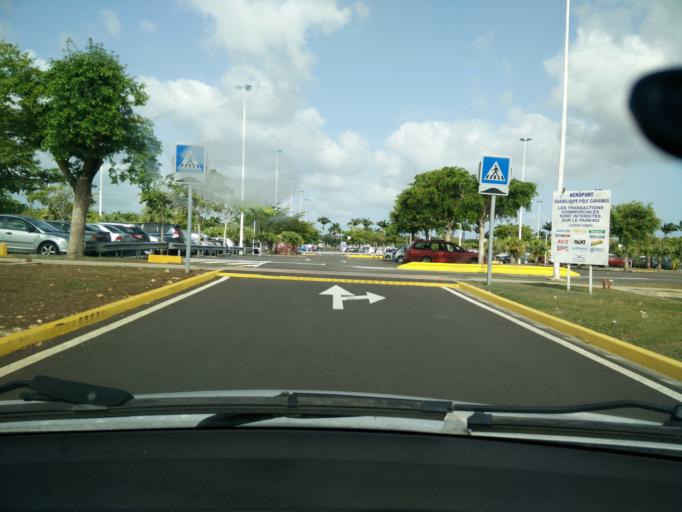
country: GP
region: Guadeloupe
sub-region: Guadeloupe
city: Les Abymes
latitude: 16.2721
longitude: -61.5274
